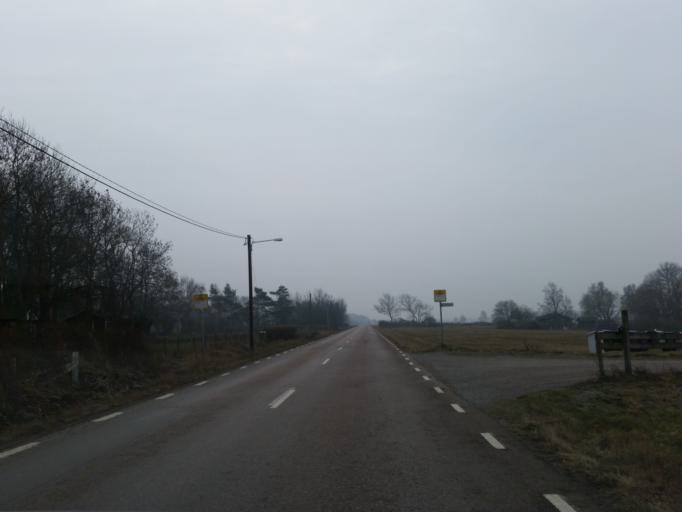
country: SE
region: Kalmar
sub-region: Morbylanga Kommun
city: Moerbylanga
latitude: 56.4176
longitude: 16.4135
